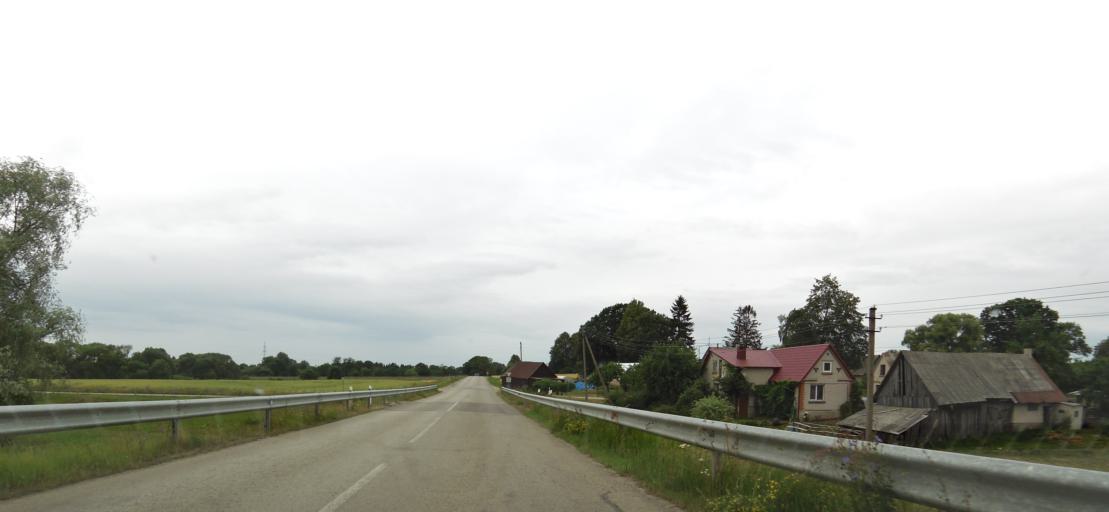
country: LT
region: Panevezys
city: Pasvalys
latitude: 56.0878
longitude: 24.4529
